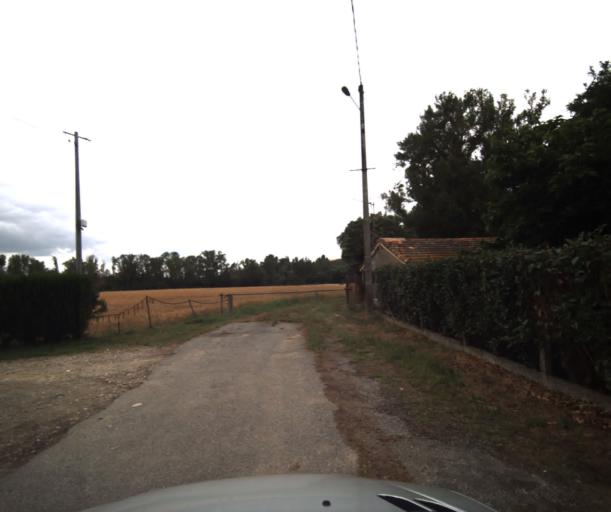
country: FR
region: Midi-Pyrenees
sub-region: Departement de la Haute-Garonne
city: Labarthe-sur-Leze
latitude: 43.4683
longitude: 1.4183
